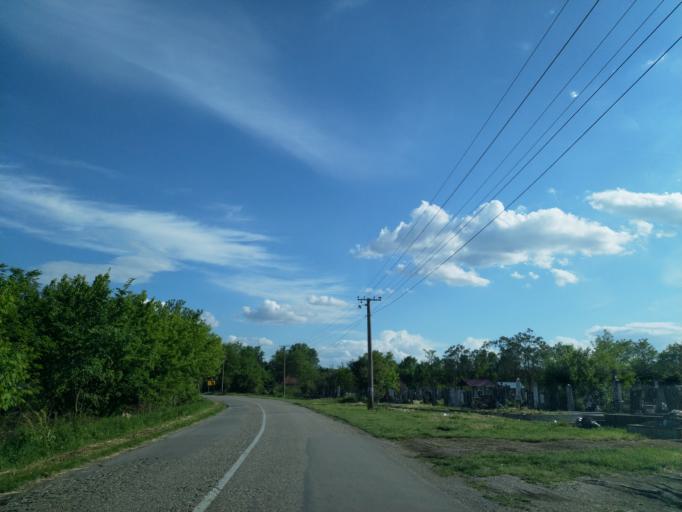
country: RS
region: Central Serbia
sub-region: Sumadijski Okrug
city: Lapovo
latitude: 44.2258
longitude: 21.0936
